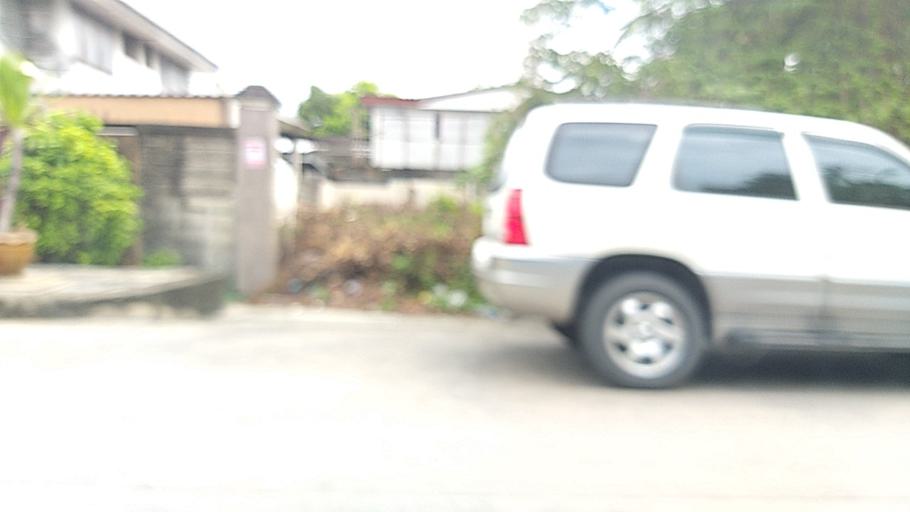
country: TH
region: Bangkok
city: Suan Luang
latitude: 13.7117
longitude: 100.6602
